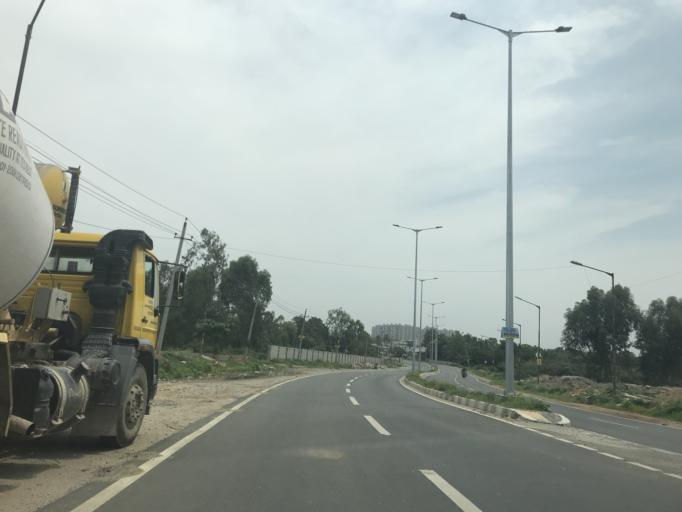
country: IN
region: Karnataka
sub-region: Bangalore Urban
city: Yelahanka
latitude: 13.0985
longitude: 77.6565
